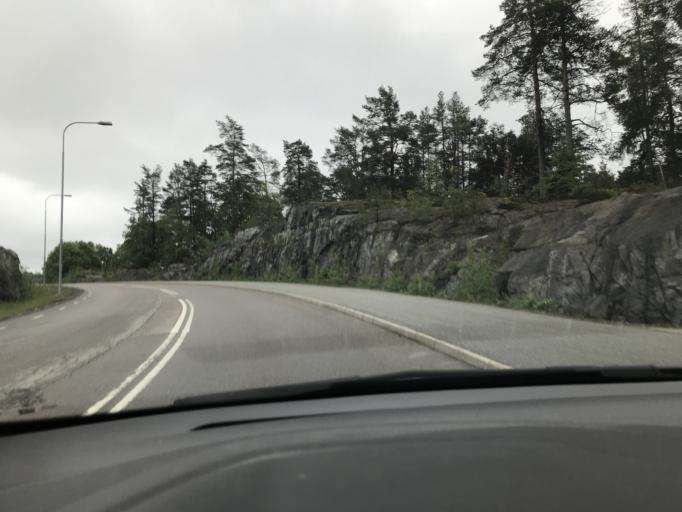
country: SE
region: Stockholm
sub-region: Botkyrka Kommun
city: Tumba
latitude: 59.2101
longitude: 17.8326
